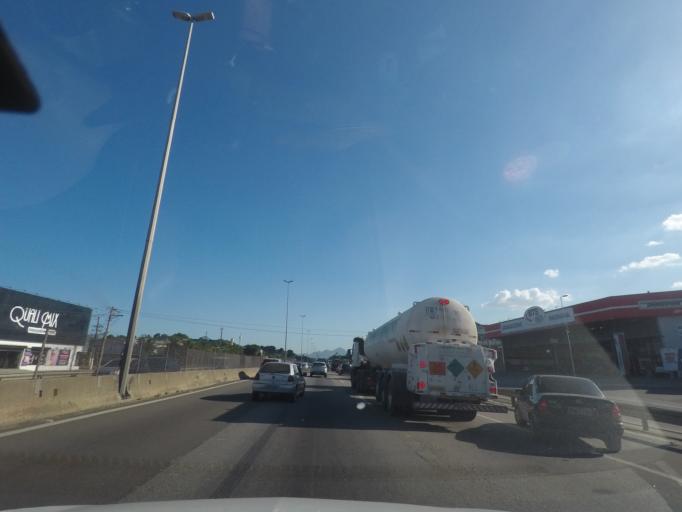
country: BR
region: Rio de Janeiro
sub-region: Duque De Caxias
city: Duque de Caxias
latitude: -22.7538
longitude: -43.2874
